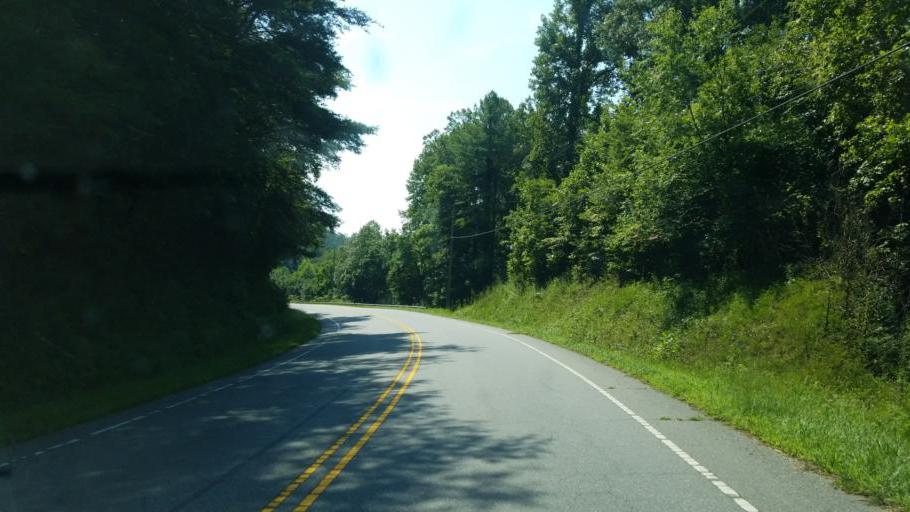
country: US
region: North Carolina
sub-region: Burke County
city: Glen Alpine
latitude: 35.8508
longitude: -81.7793
